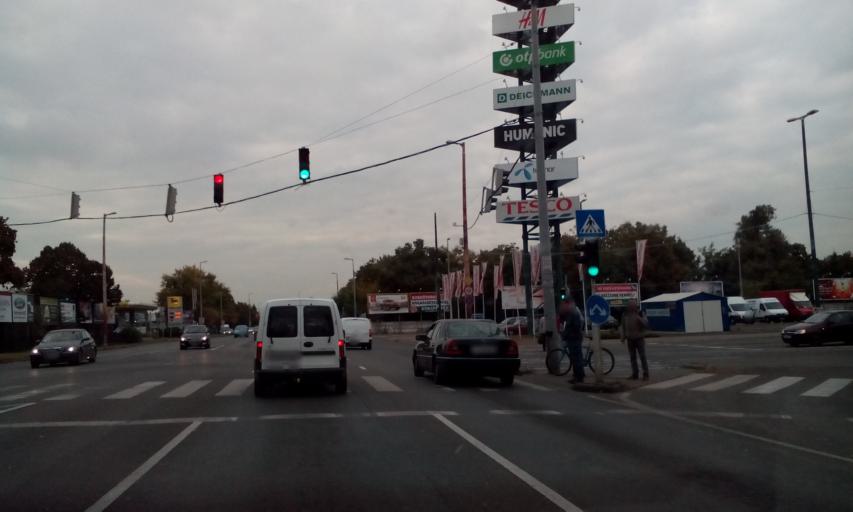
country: HU
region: Budapest
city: Budapest XV. keruelet
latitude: 47.5502
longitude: 19.1379
